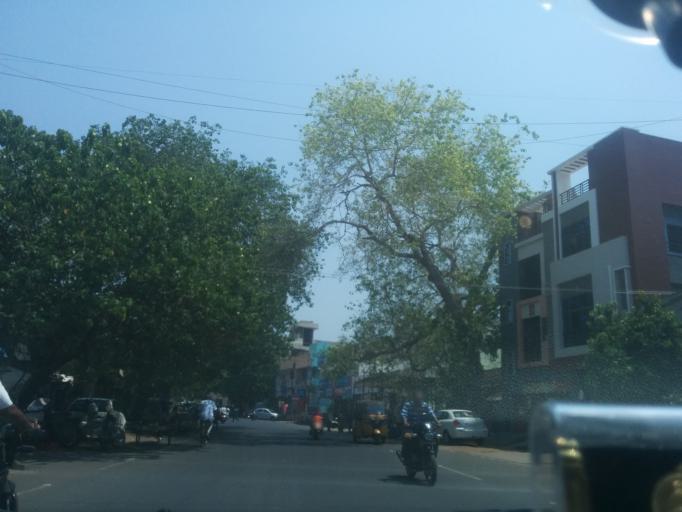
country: IN
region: Andhra Pradesh
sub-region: East Godavari
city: Rajahmundry
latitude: 17.0197
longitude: 81.7742
